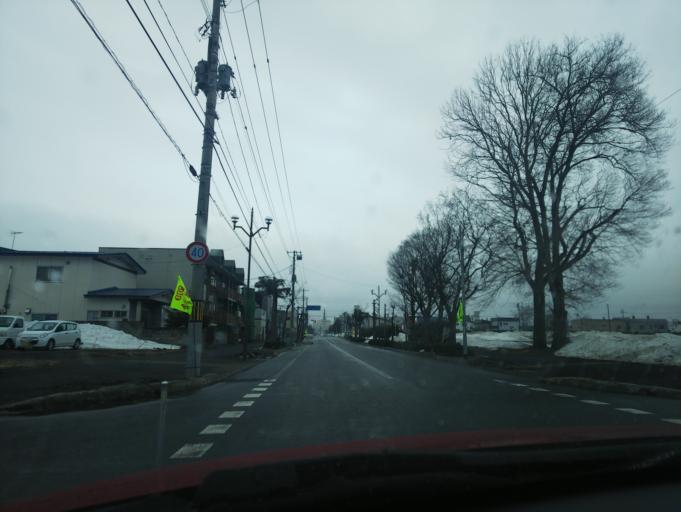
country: JP
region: Hokkaido
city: Nayoro
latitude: 44.3475
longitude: 142.4605
